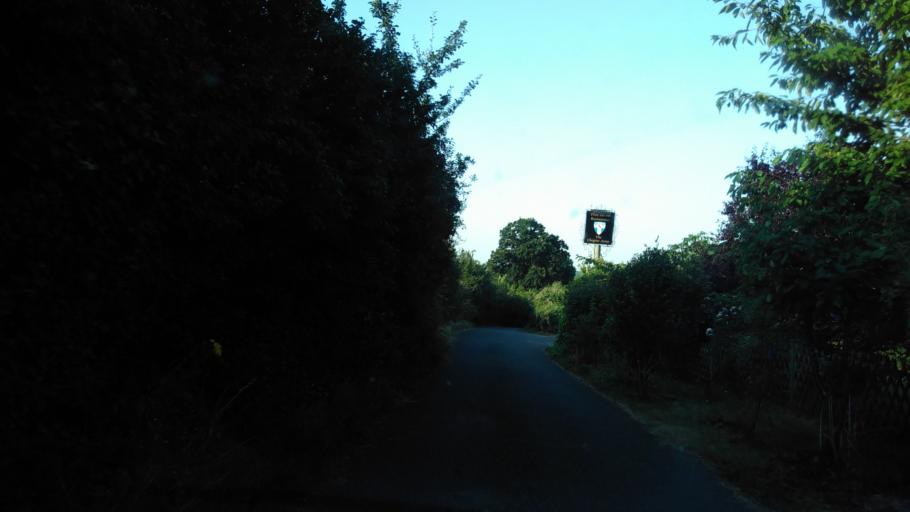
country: GB
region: England
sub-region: Kent
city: Chartham
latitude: 51.2690
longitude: 1.0143
